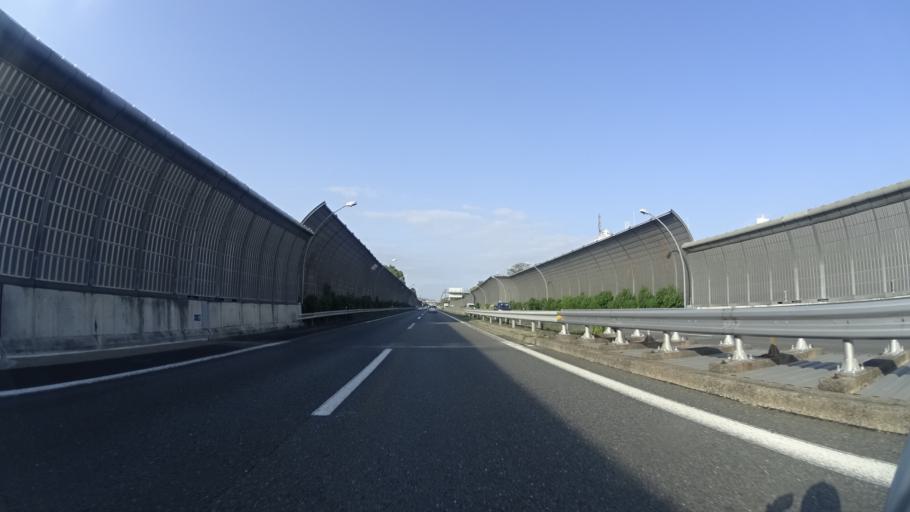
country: JP
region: Osaka
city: Suita
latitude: 34.7876
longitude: 135.5317
